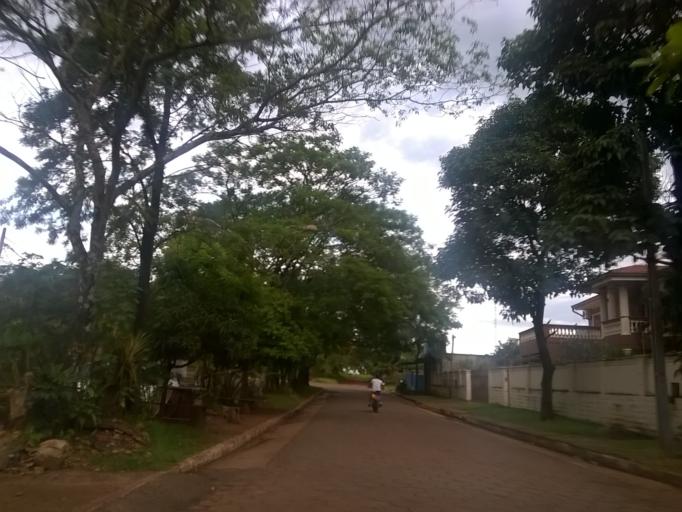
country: PY
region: Alto Parana
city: Presidente Franco
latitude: -25.5416
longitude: -54.6265
